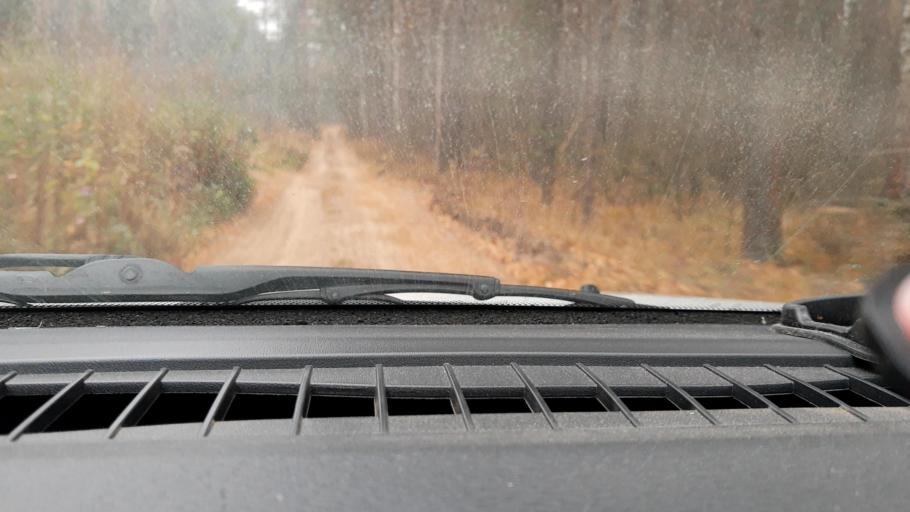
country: RU
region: Nizjnij Novgorod
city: Sitniki
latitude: 56.4316
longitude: 44.0623
